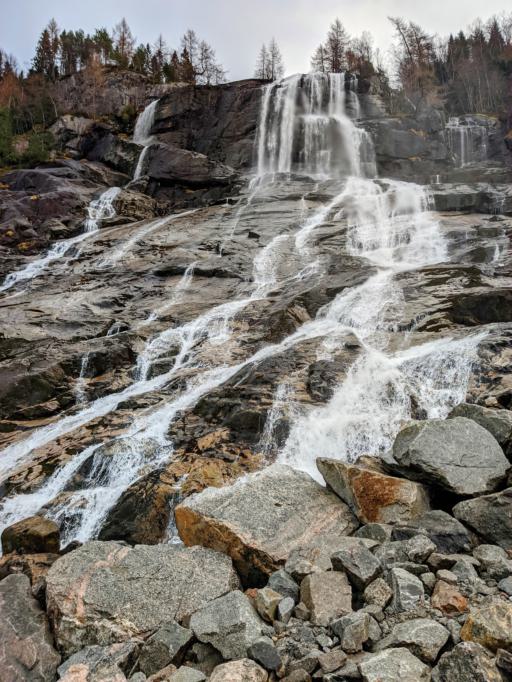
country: NO
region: Hordaland
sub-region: Kvinnherad
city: Rosendal
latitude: 60.1001
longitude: 6.1685
